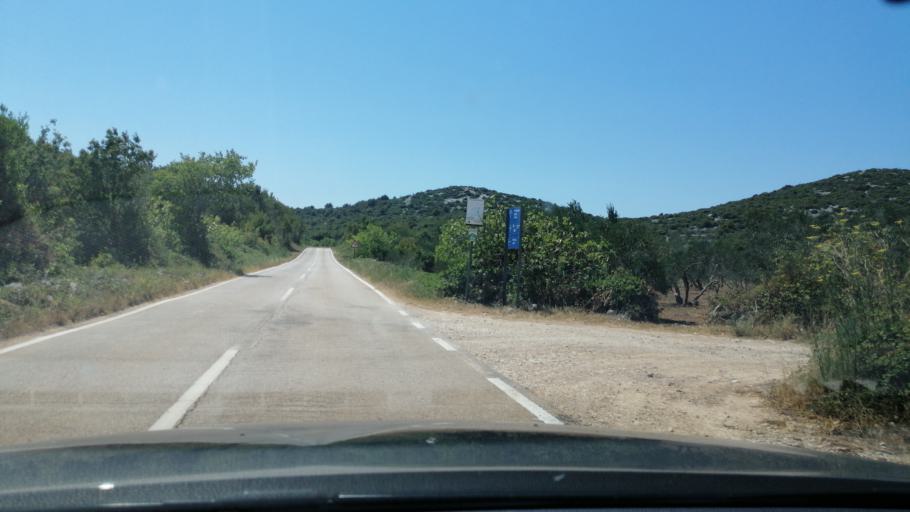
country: HR
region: Sibensko-Kniniska
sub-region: Grad Sibenik
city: Pirovac
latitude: 43.8473
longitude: 15.6868
